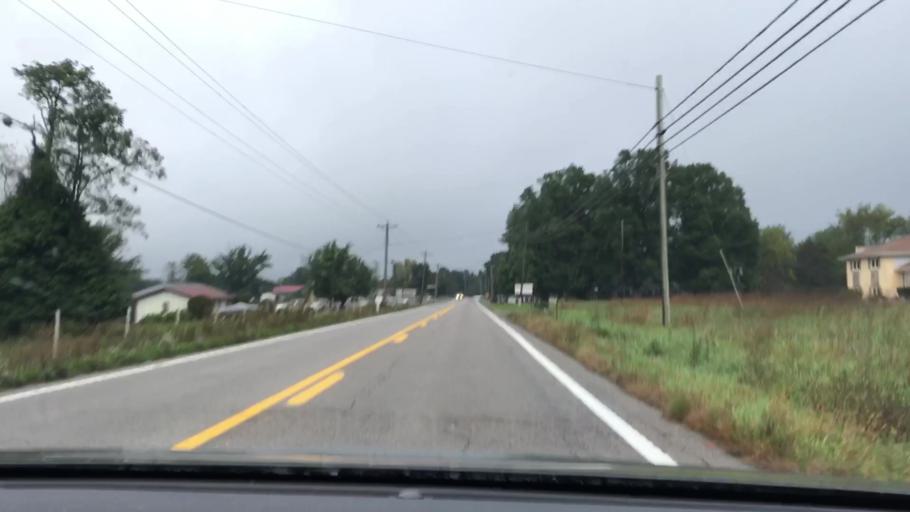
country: US
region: Tennessee
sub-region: Fentress County
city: Grimsley
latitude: 36.2299
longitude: -85.0088
